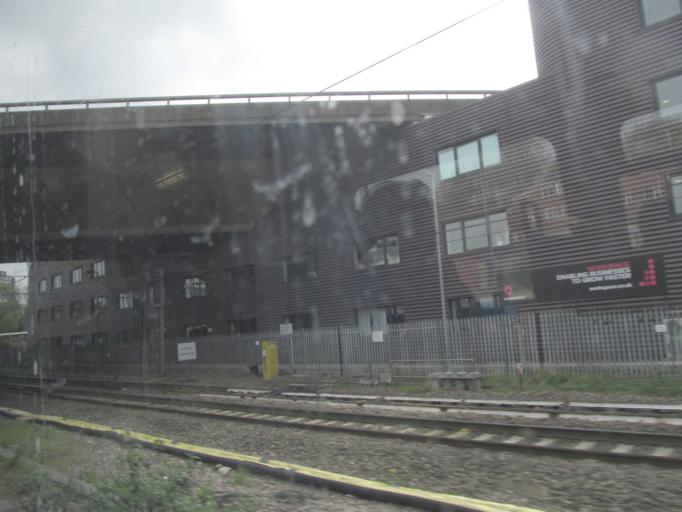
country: GB
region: England
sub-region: Greater London
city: Bayswater
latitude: 51.5217
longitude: -0.2030
